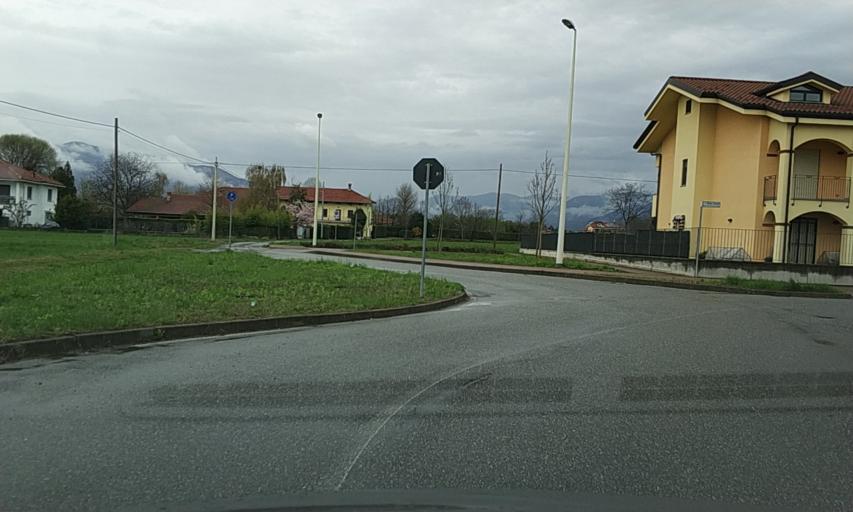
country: IT
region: Piedmont
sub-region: Provincia di Torino
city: Cirie
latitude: 45.2378
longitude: 7.5874
